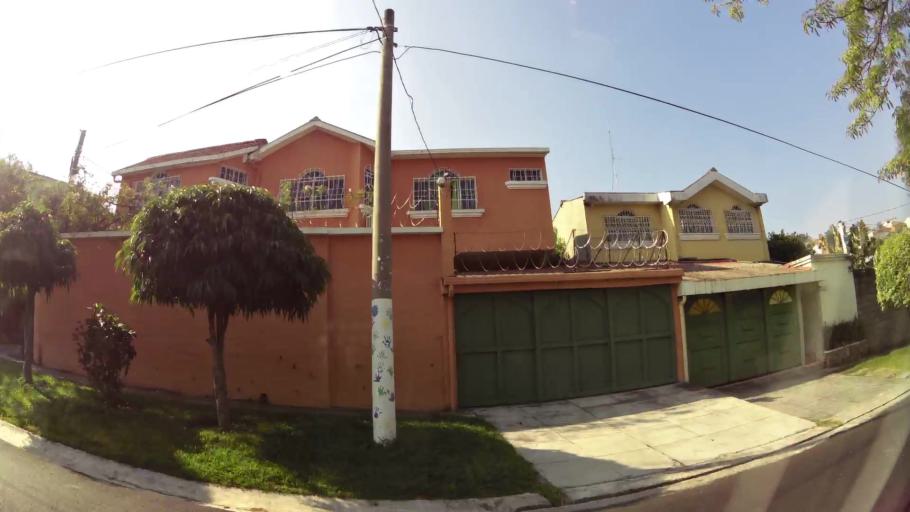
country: SV
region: La Libertad
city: Antiguo Cuscatlan
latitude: 13.6695
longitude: -89.2305
